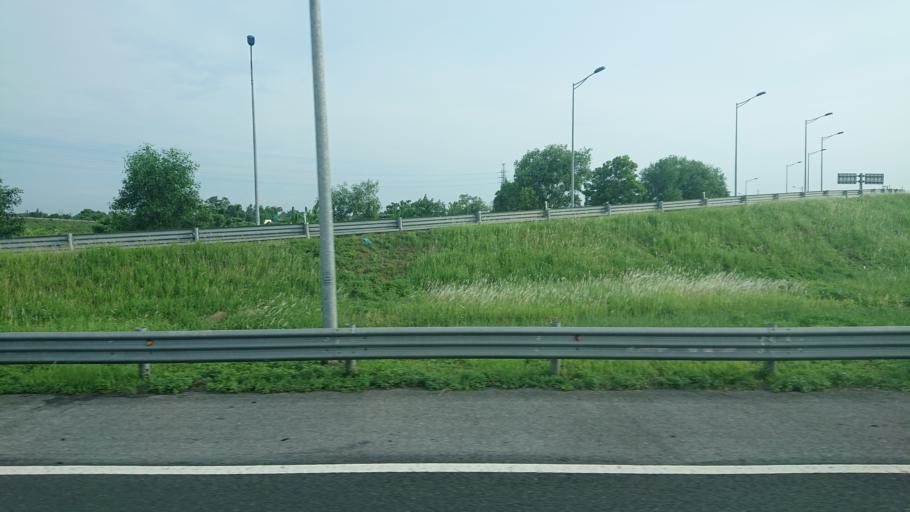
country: VN
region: Hai Phong
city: An Lao
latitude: 20.8029
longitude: 106.5258
